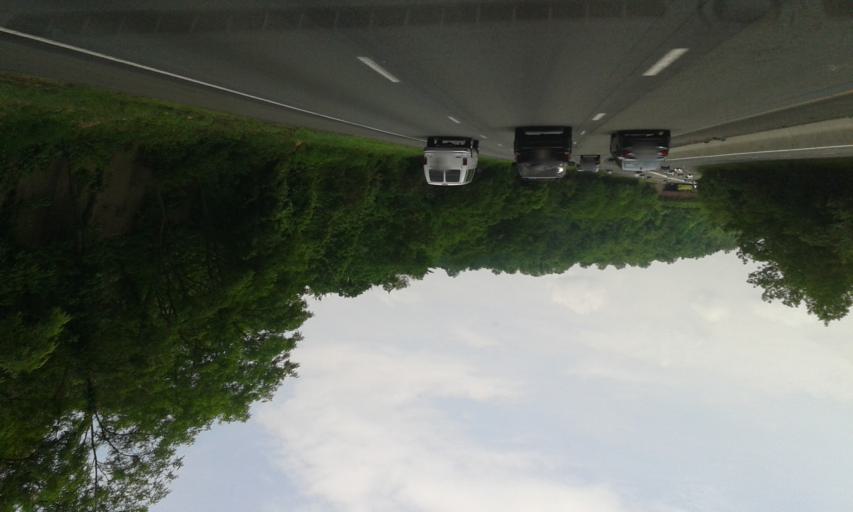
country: US
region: New Jersey
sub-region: Union County
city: Mountainside
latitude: 40.6998
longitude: -74.3589
